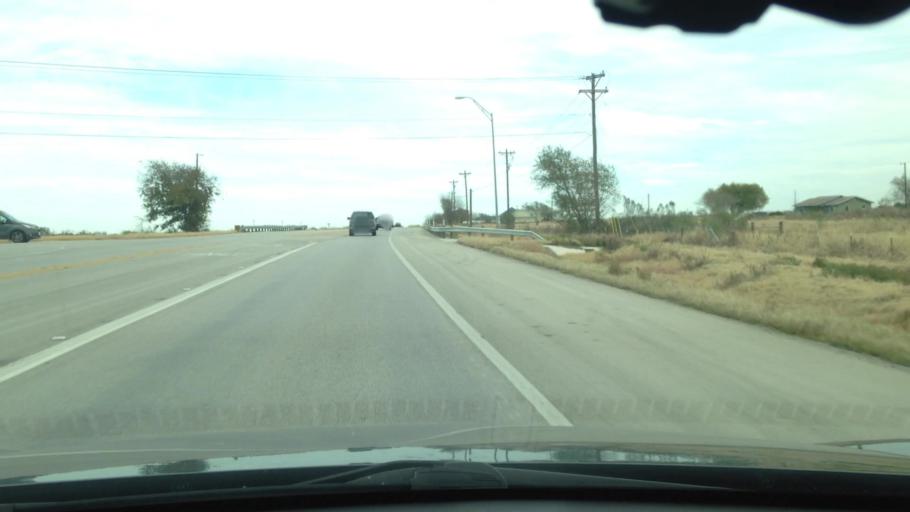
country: US
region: Texas
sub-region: Caldwell County
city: Martindale
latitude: 29.9157
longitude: -97.8497
